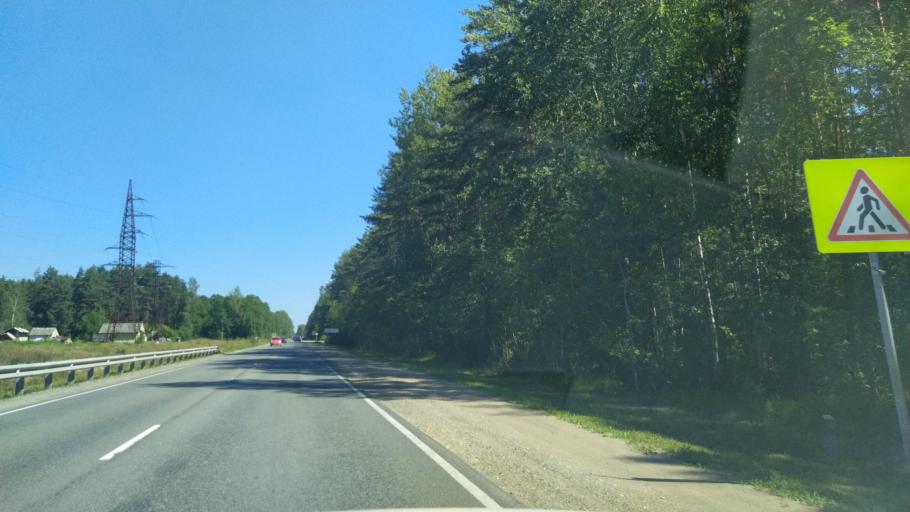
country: RU
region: Leningrad
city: Imeni Morozova
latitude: 59.9610
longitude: 31.0068
